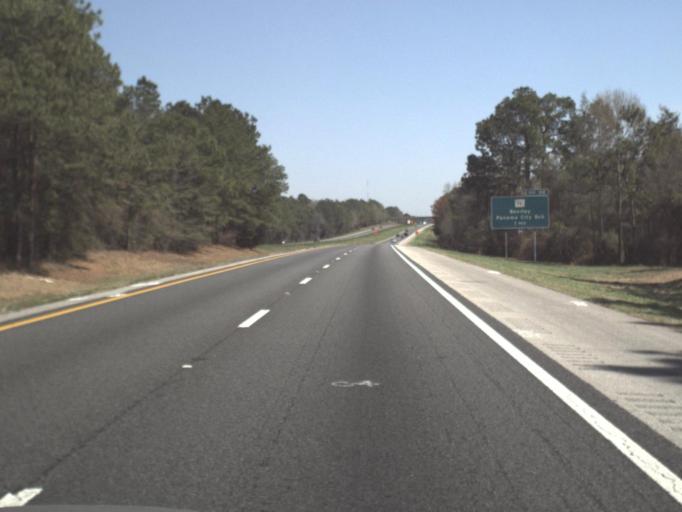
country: US
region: Florida
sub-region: Holmes County
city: Bonifay
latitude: 30.7630
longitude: -85.7073
